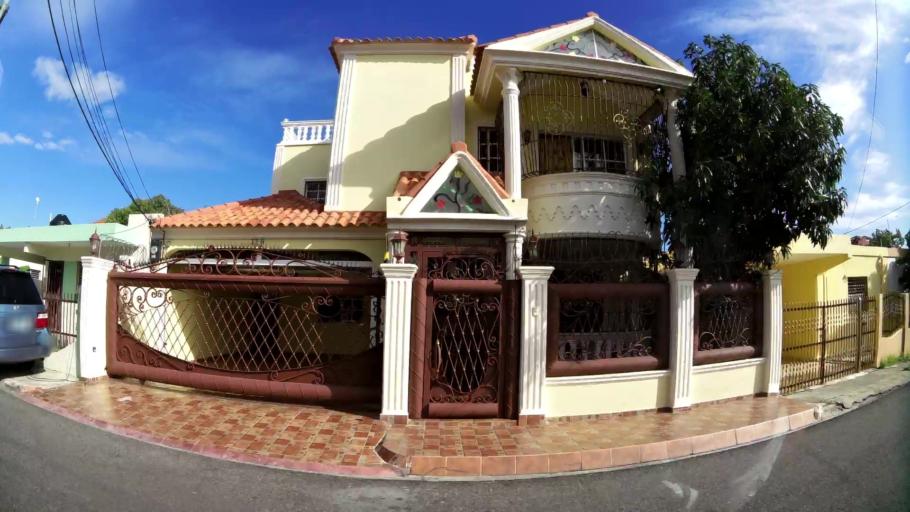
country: DO
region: Santo Domingo
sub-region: Santo Domingo
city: Santo Domingo Este
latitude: 18.4860
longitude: -69.8603
